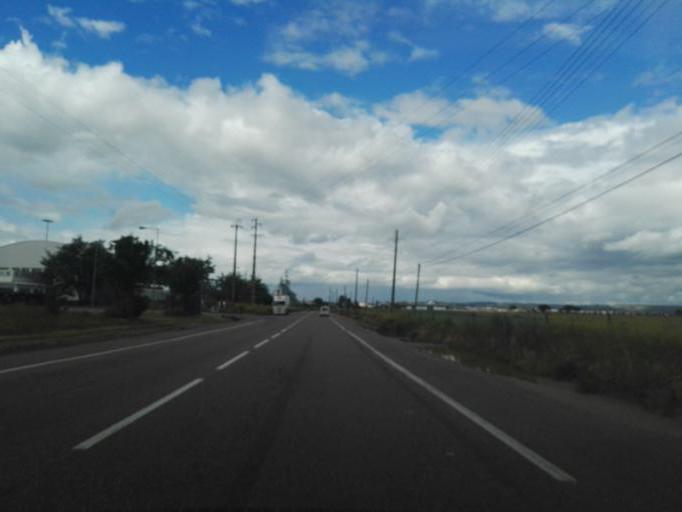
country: PT
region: Santarem
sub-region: Torres Novas
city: Riachos
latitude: 39.4356
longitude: -8.4974
